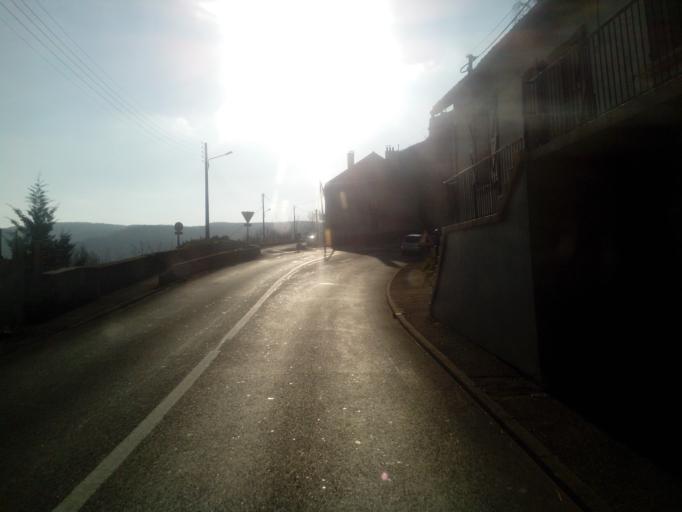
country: FR
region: Midi-Pyrenees
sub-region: Departement de l'Aveyron
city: Capdenac-Gare
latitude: 44.5757
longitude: 2.0705
